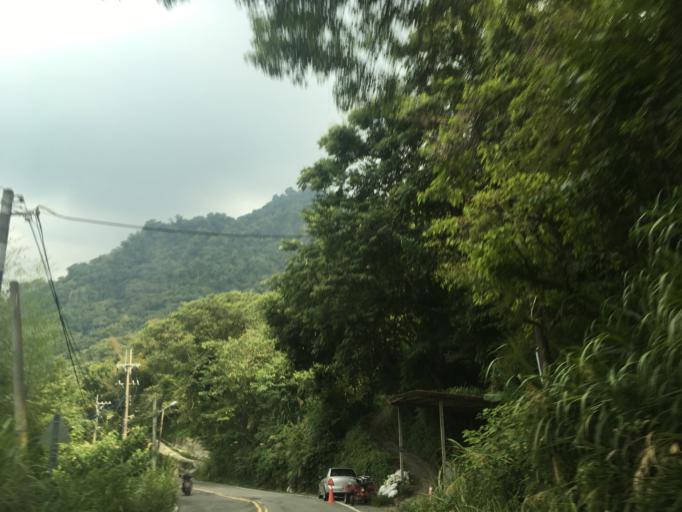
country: TW
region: Taiwan
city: Fengyuan
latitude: 24.3356
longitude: 120.9298
